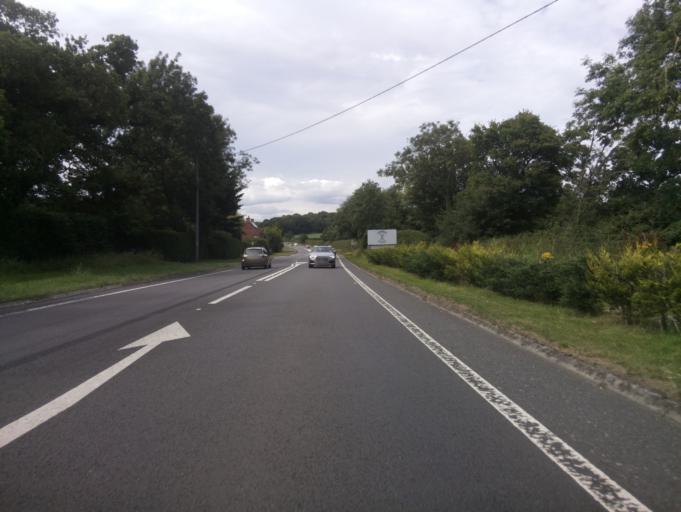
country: GB
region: England
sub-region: Somerset
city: Yeovil
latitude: 50.8694
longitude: -2.5961
